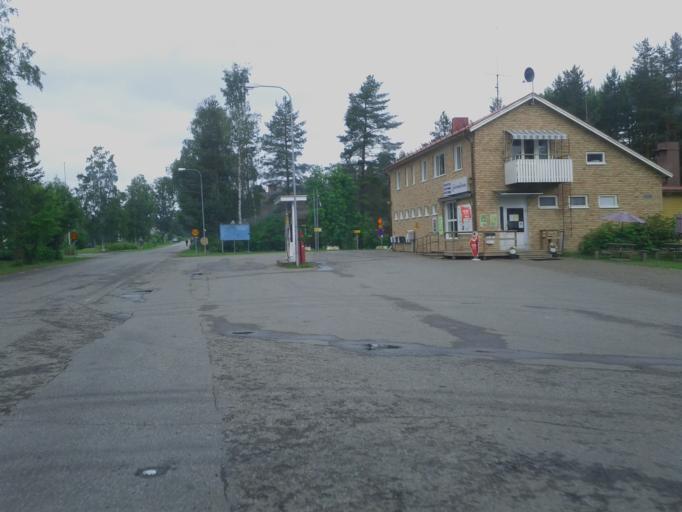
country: SE
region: Vaesterbotten
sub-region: Skelleftea Kommun
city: Kage
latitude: 64.9179
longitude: 20.9547
